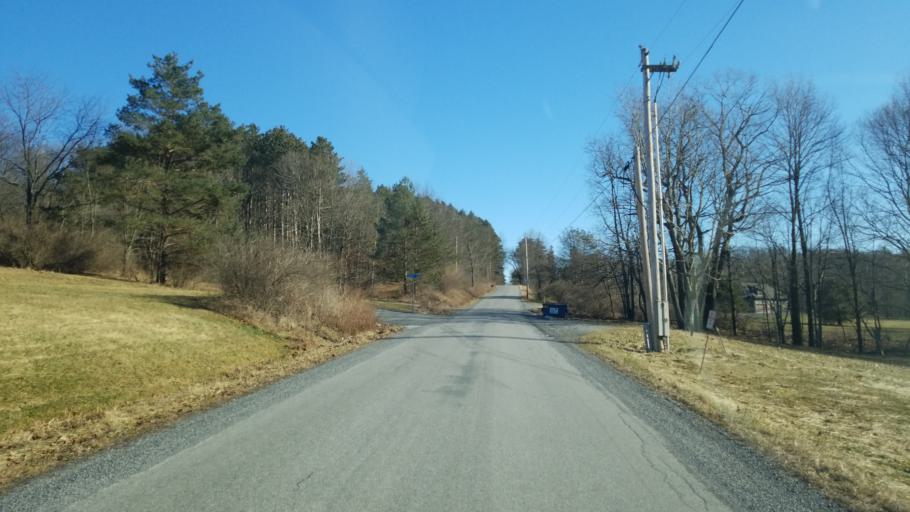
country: US
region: Pennsylvania
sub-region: Jefferson County
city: Sykesville
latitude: 41.0503
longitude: -78.7916
